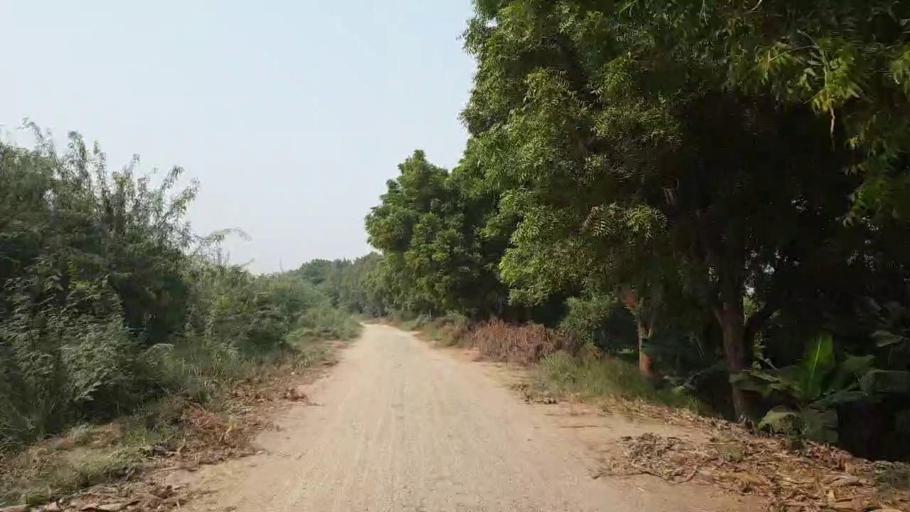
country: PK
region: Sindh
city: Tando Muhammad Khan
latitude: 25.1882
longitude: 68.5951
